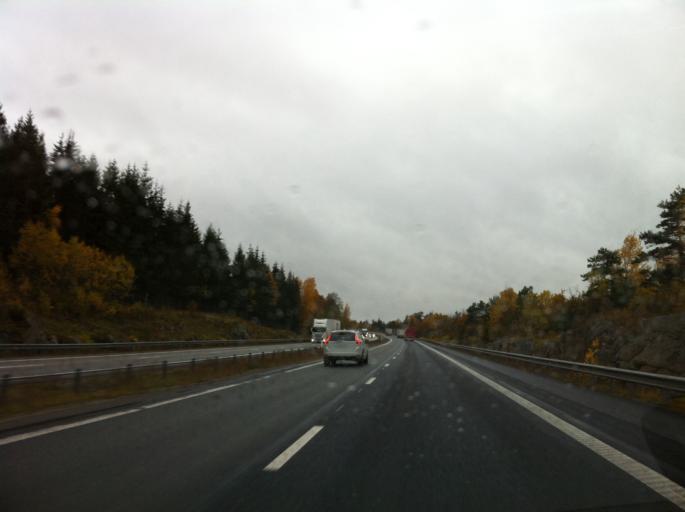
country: SE
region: Joenkoeping
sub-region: Jonkopings Kommun
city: Kaxholmen
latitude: 57.9646
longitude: 14.3604
